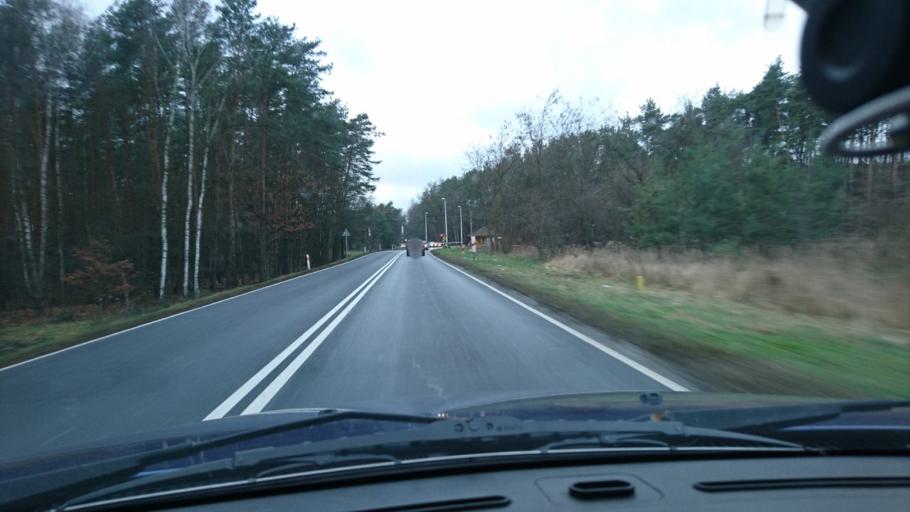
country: PL
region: Opole Voivodeship
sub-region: Powiat kluczborski
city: Kluczbork
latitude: 50.9575
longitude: 18.3074
